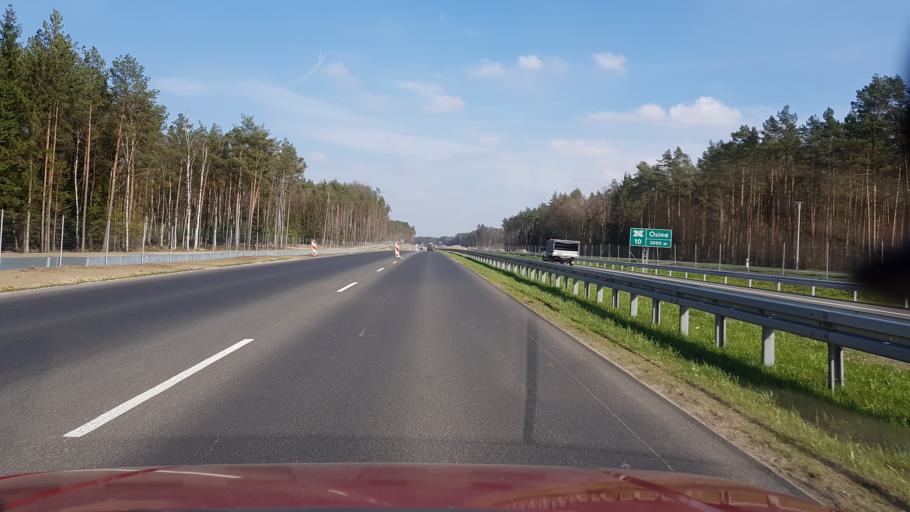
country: PL
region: West Pomeranian Voivodeship
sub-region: Powiat goleniowski
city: Osina
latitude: 53.6187
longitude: 14.9497
